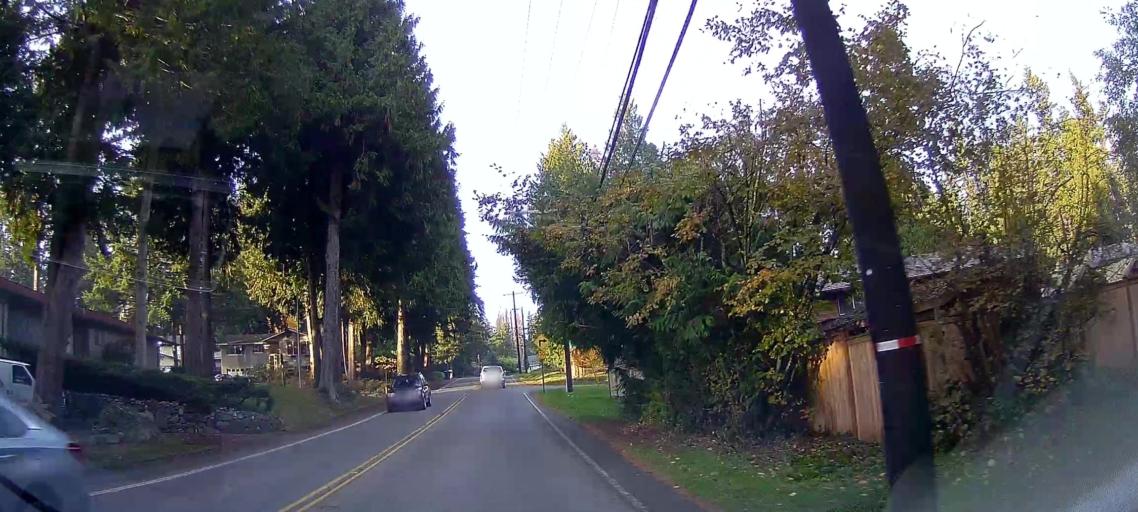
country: US
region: Washington
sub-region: Snohomish County
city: Alderwood Manor
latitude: 47.8098
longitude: -122.2602
